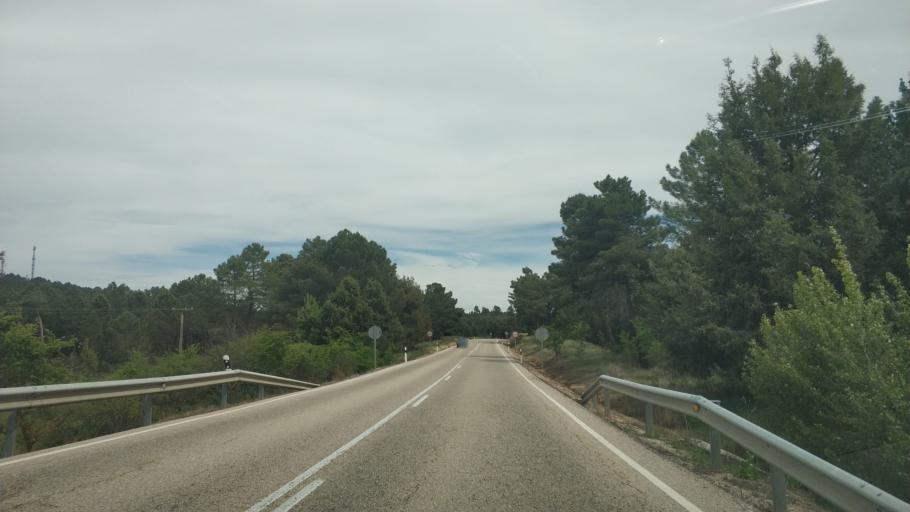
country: ES
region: Castille and Leon
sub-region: Provincia de Soria
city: Valdenebro
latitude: 41.5574
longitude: -2.9680
